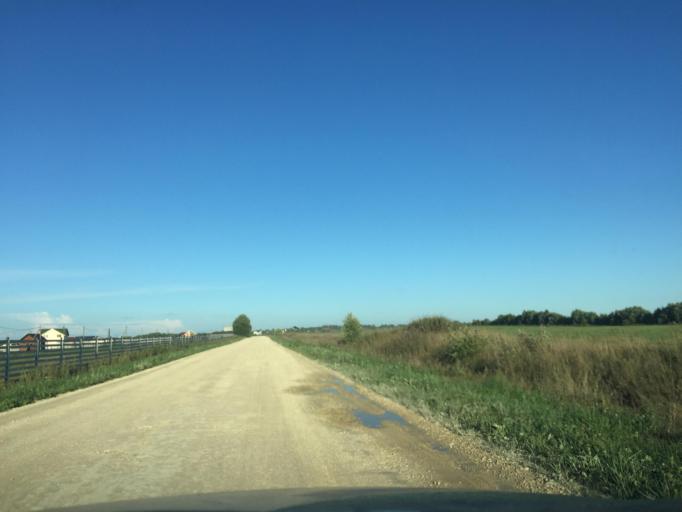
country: RU
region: Leningrad
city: Rozhdestveno
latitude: 59.3327
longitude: 30.0034
